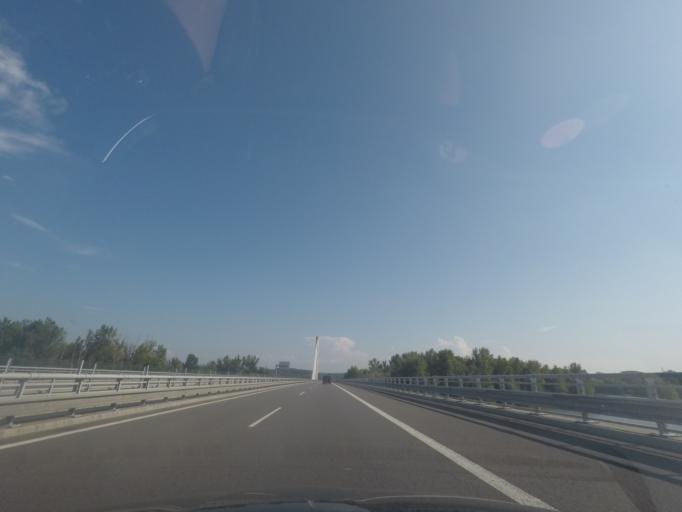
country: PL
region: Silesian Voivodeship
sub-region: Powiat raciborski
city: Chalupki
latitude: 49.8905
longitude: 18.3040
